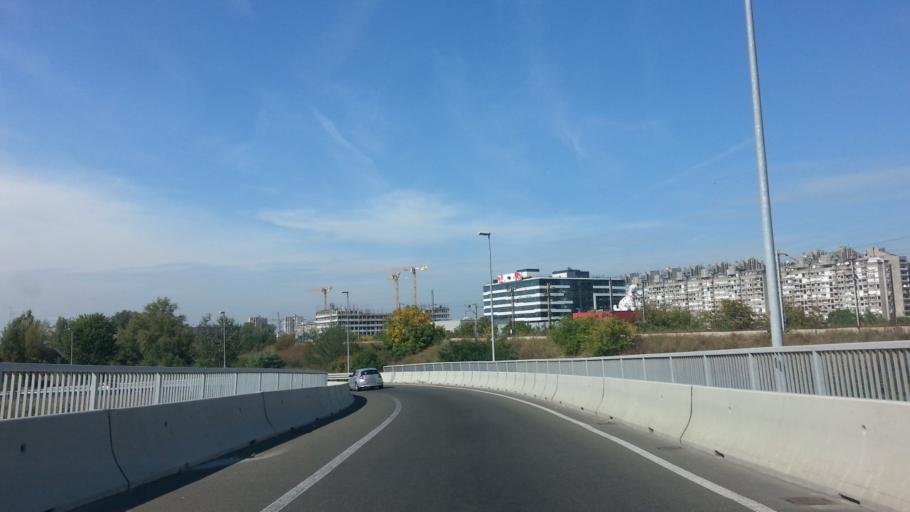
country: RS
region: Central Serbia
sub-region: Belgrade
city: Novi Beograd
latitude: 44.8035
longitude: 20.4238
